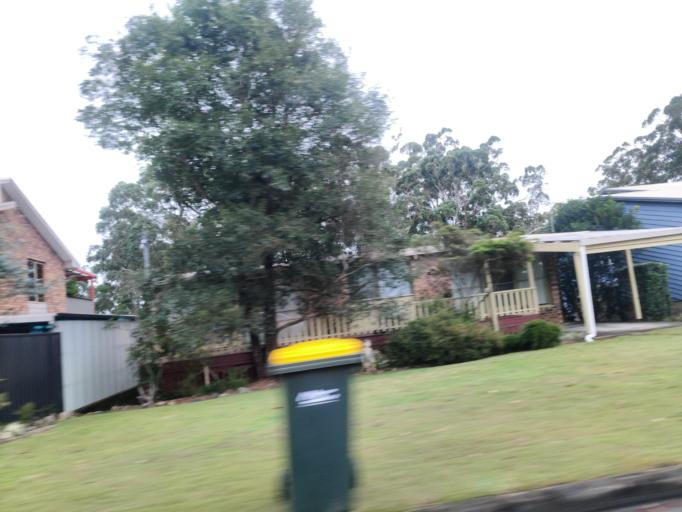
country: AU
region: New South Wales
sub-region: Great Lakes
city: Forster
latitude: -32.3771
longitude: 152.5030
